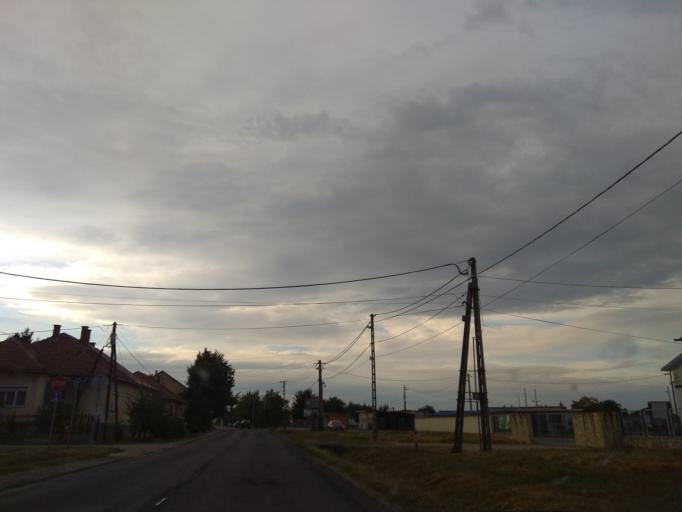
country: HU
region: Borsod-Abauj-Zemplen
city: Miskolc
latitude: 48.0856
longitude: 20.8172
